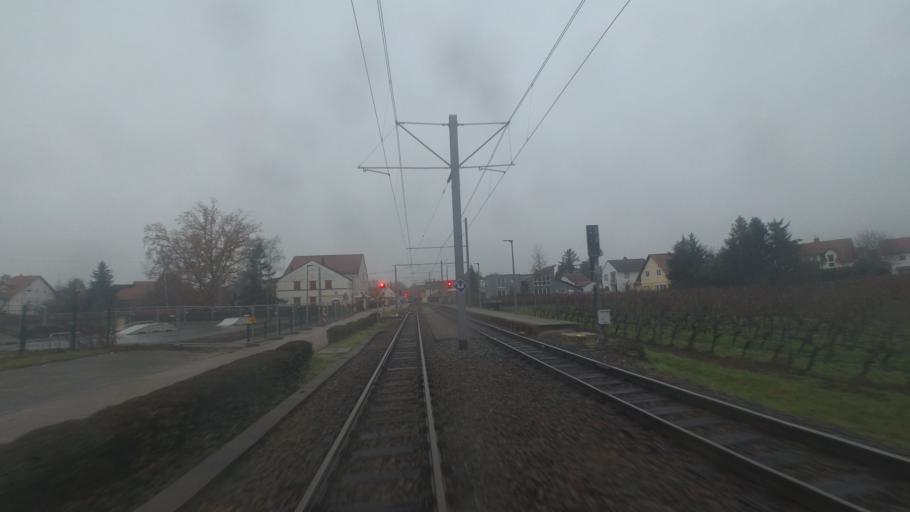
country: DE
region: Rheinland-Pfalz
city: Ellerstadt
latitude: 49.4642
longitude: 8.2654
